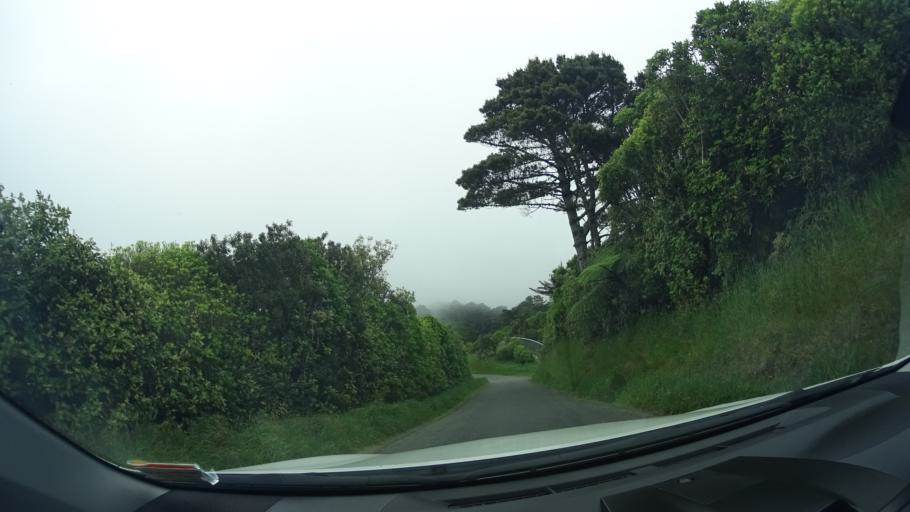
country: NZ
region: Wellington
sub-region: Wellington City
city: Brooklyn
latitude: -41.3067
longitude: 174.7475
